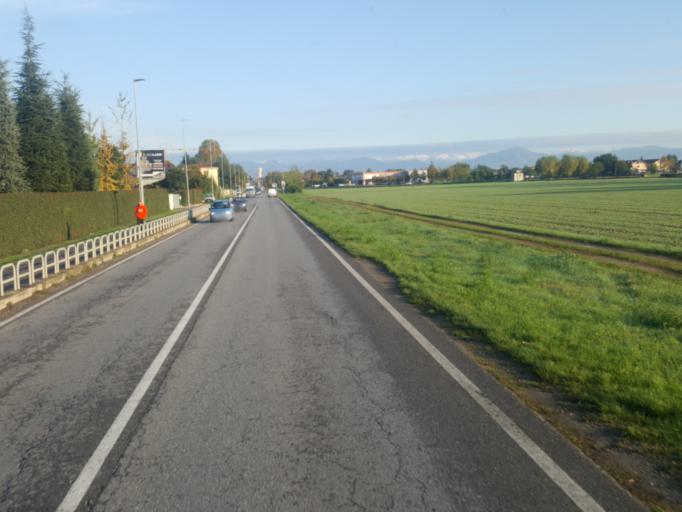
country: IT
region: Lombardy
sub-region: Provincia di Bergamo
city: Cologno al Serio
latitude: 45.5686
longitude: 9.7085
